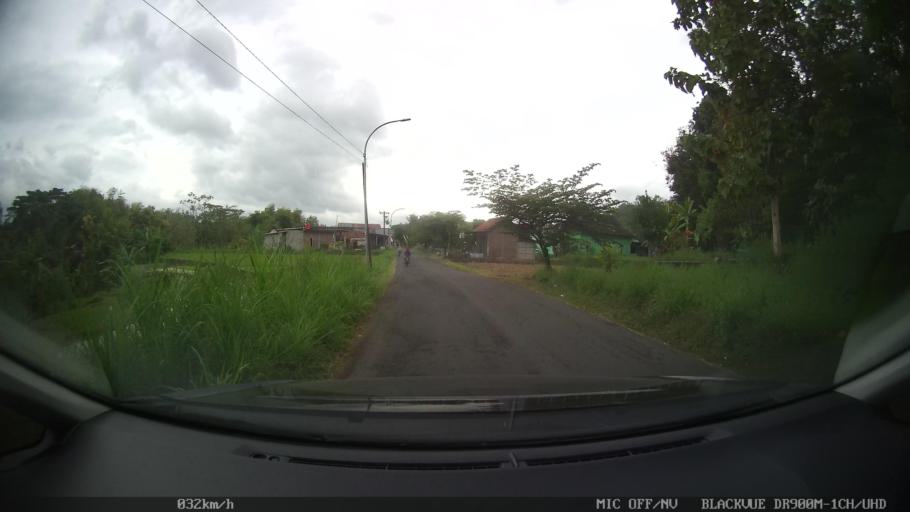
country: ID
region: Daerah Istimewa Yogyakarta
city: Sewon
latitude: -7.8616
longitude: 110.4216
